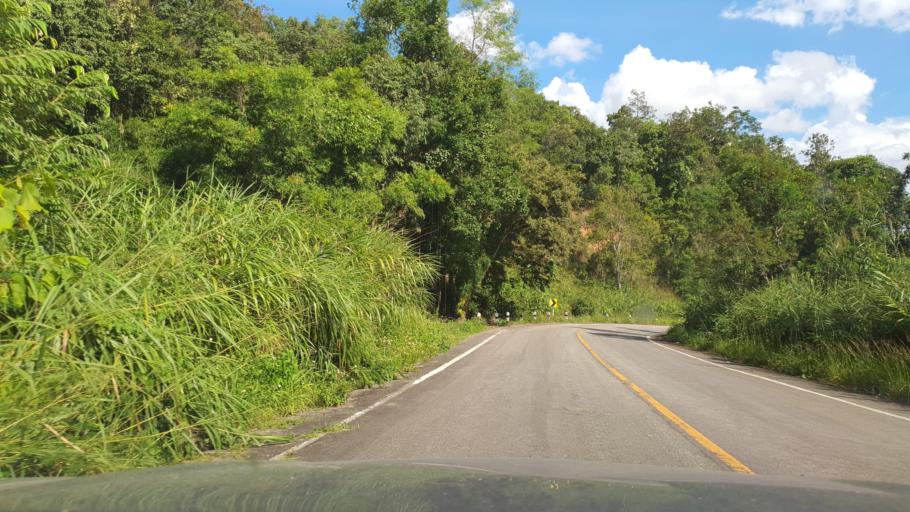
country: TH
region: Chiang Rai
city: Wiang Pa Pao
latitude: 19.3331
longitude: 99.4588
